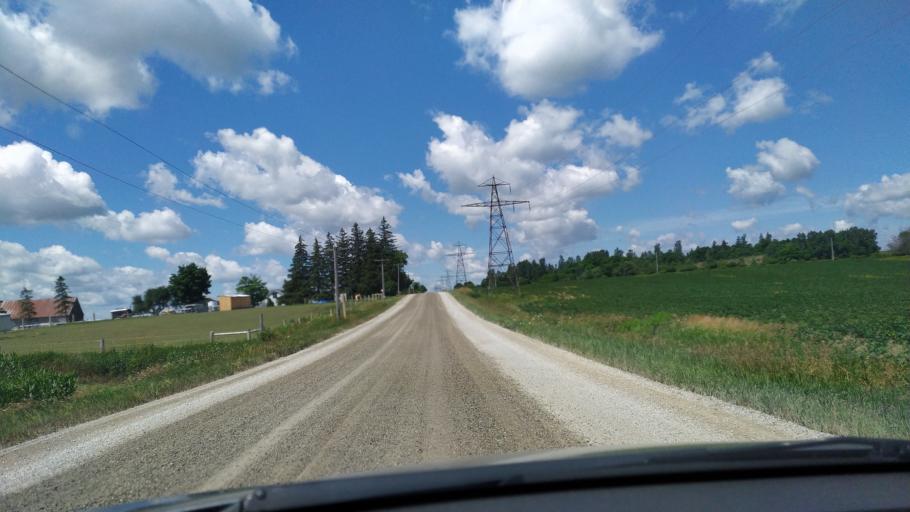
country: CA
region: Ontario
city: Stratford
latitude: 43.3878
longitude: -80.8203
